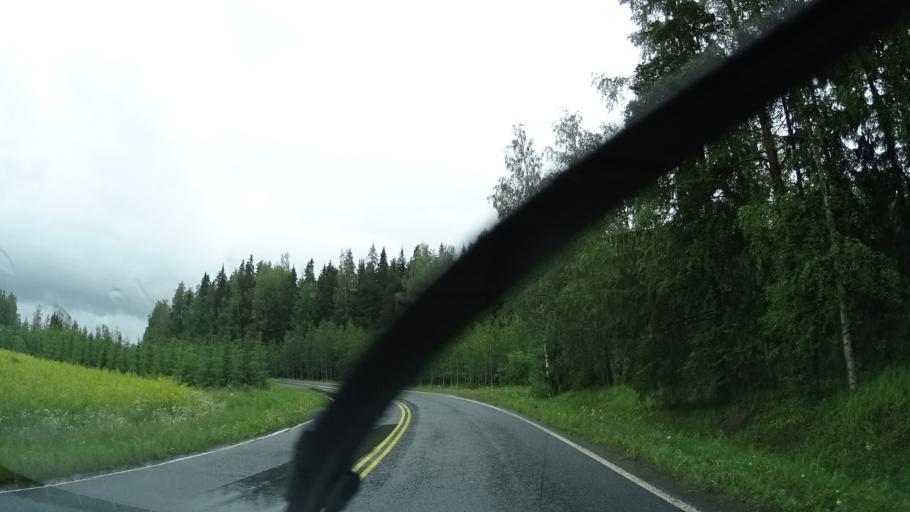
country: FI
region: Haeme
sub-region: Forssa
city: Humppila
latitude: 60.9916
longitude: 23.2569
